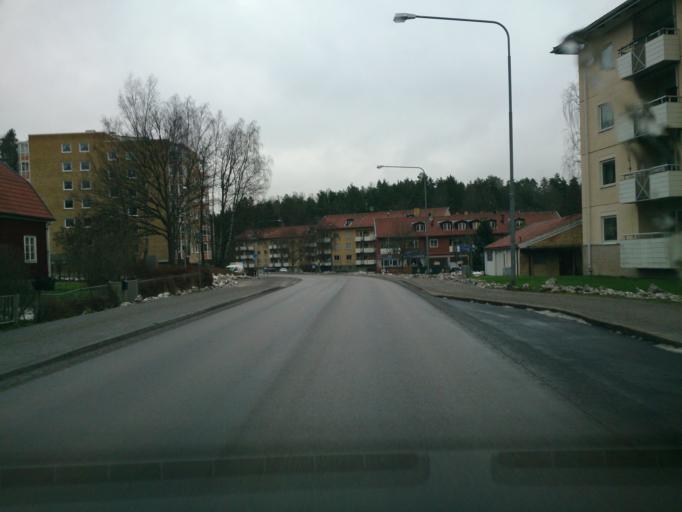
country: SE
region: OEstergoetland
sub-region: Atvidabergs Kommun
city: Atvidaberg
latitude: 58.2040
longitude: 16.0071
